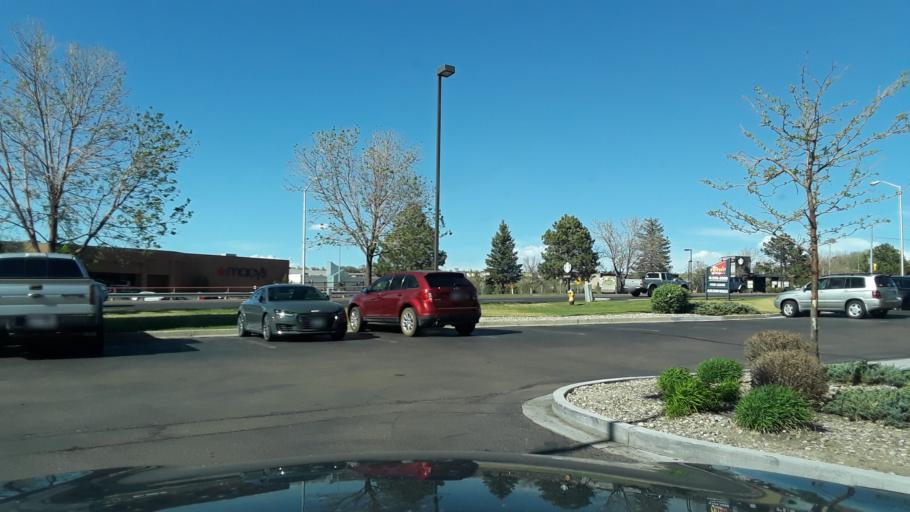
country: US
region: Colorado
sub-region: El Paso County
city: Air Force Academy
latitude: 38.9448
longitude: -104.7952
